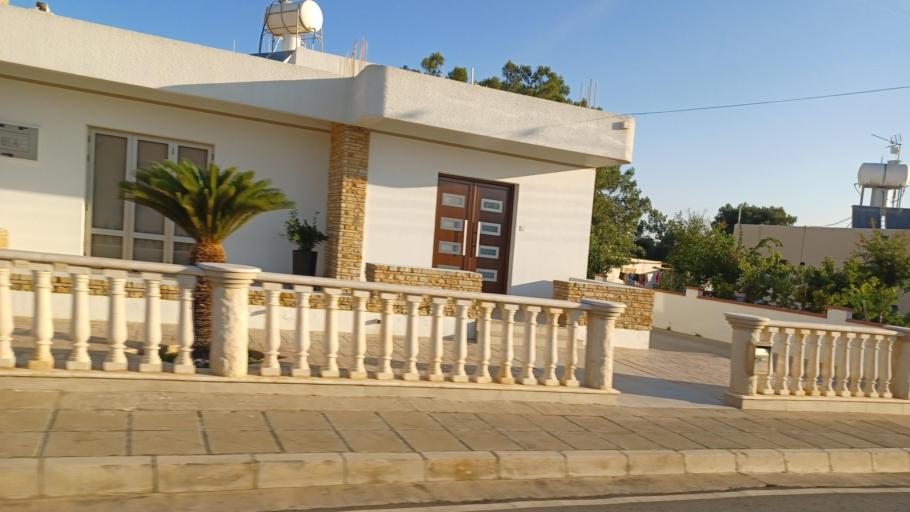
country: CY
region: Ammochostos
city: Achna
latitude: 35.0324
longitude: 33.7707
